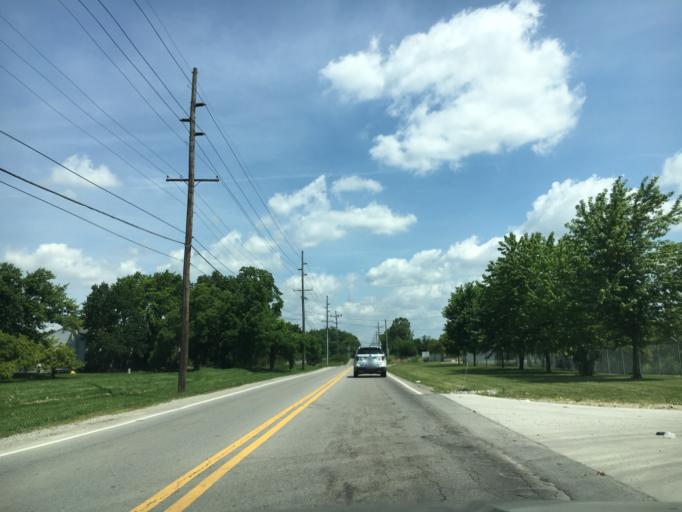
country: US
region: Ohio
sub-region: Franklin County
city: Lincoln Village
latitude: 39.9225
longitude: -83.1441
